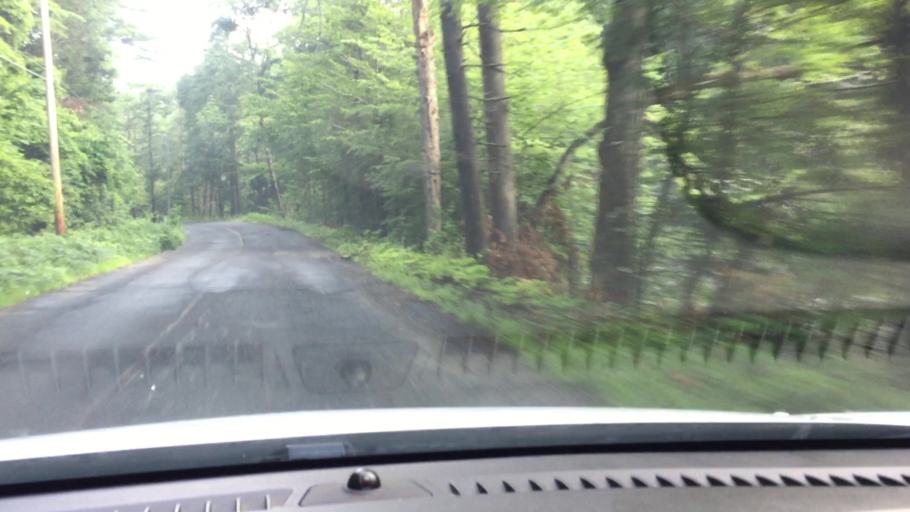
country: US
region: Massachusetts
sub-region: Hampshire County
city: Chesterfield
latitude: 42.3089
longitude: -72.9123
